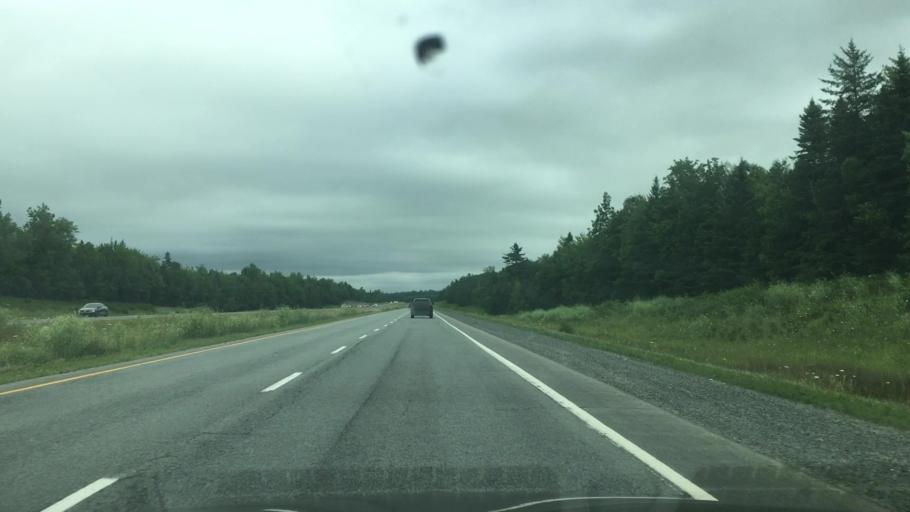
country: CA
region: Nova Scotia
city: Cole Harbour
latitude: 45.0087
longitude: -63.4800
